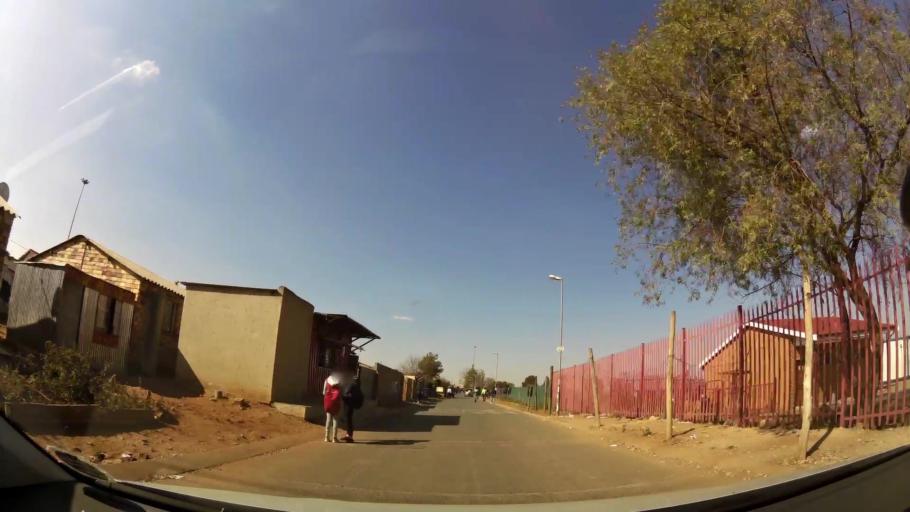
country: ZA
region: Gauteng
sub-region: City of Johannesburg Metropolitan Municipality
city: Soweto
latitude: -26.2851
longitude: 27.8563
